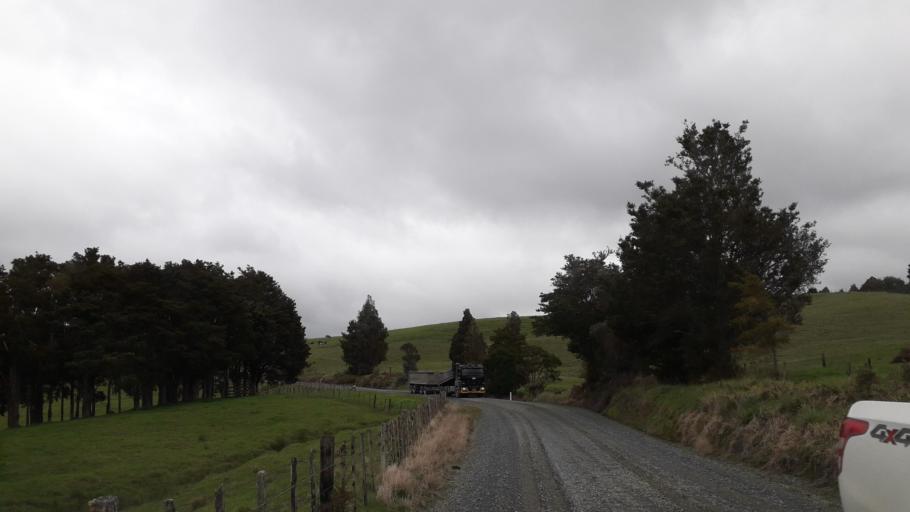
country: NZ
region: Northland
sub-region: Far North District
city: Waimate North
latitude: -35.1378
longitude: 173.7128
